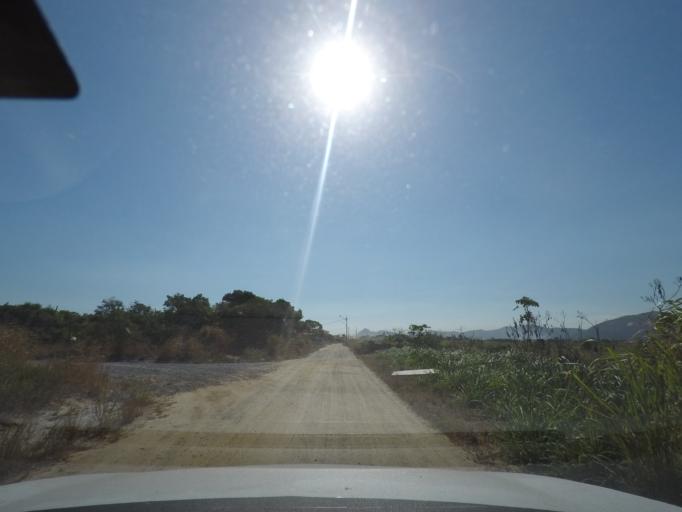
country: BR
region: Rio de Janeiro
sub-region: Marica
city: Marica
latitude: -22.9656
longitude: -42.9162
